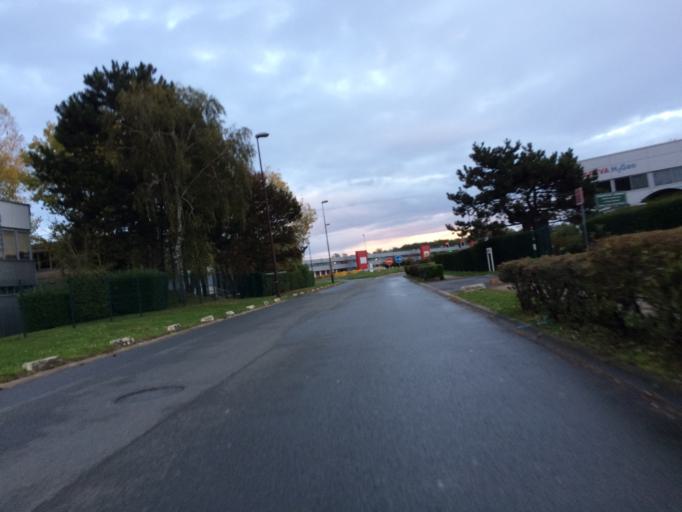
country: FR
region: Ile-de-France
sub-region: Departement de l'Essonne
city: Orsay
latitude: 48.6804
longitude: 2.1997
